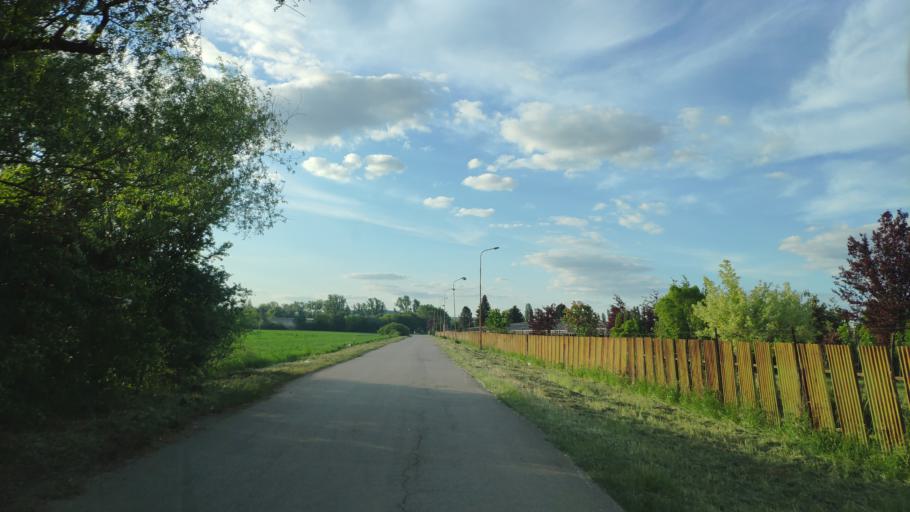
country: SK
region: Kosicky
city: Kosice
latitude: 48.6540
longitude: 21.3168
